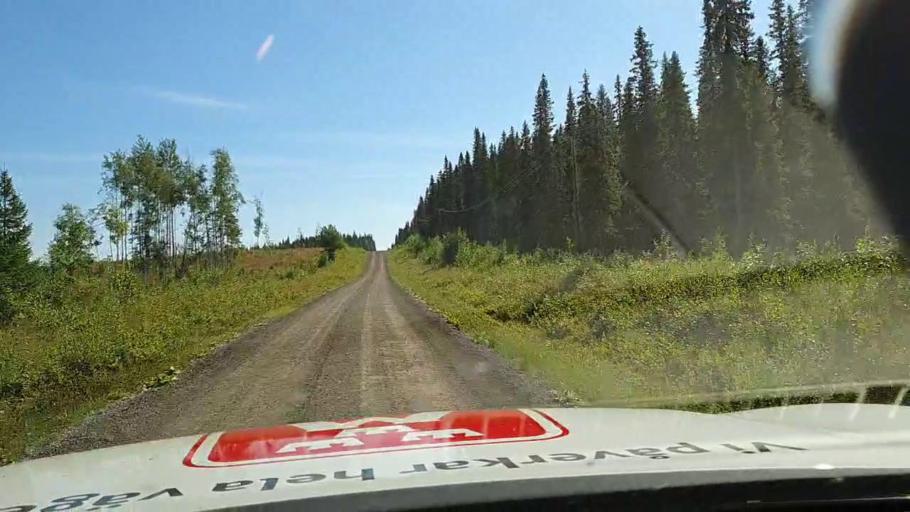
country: SE
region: Jaemtland
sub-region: Stroemsunds Kommun
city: Stroemsund
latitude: 63.7856
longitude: 15.3023
